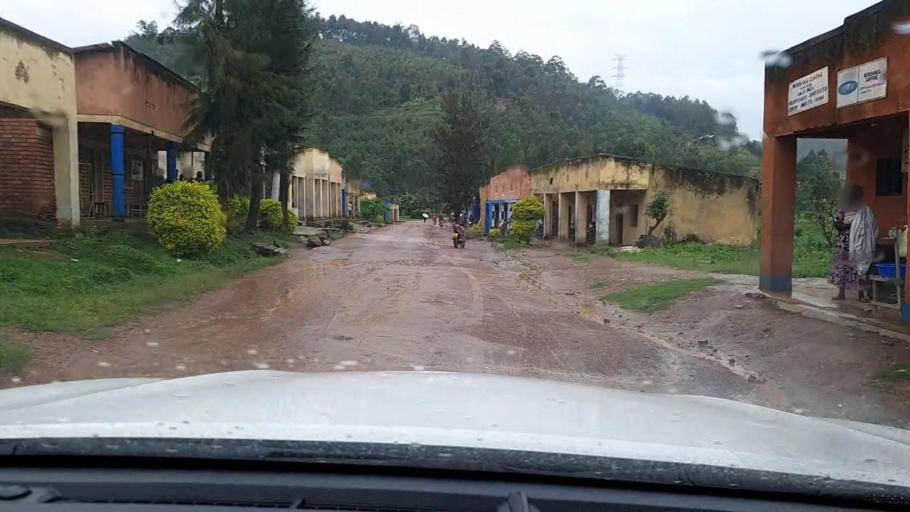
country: RW
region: Northern Province
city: Byumba
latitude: -1.7246
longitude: 29.9308
